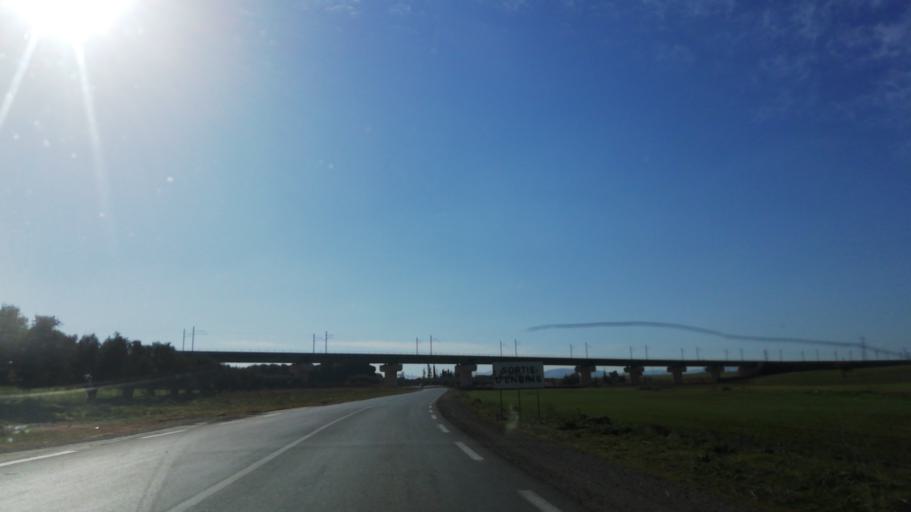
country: DZ
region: Tlemcen
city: Ouled Mimoun
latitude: 35.0091
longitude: -0.9063
